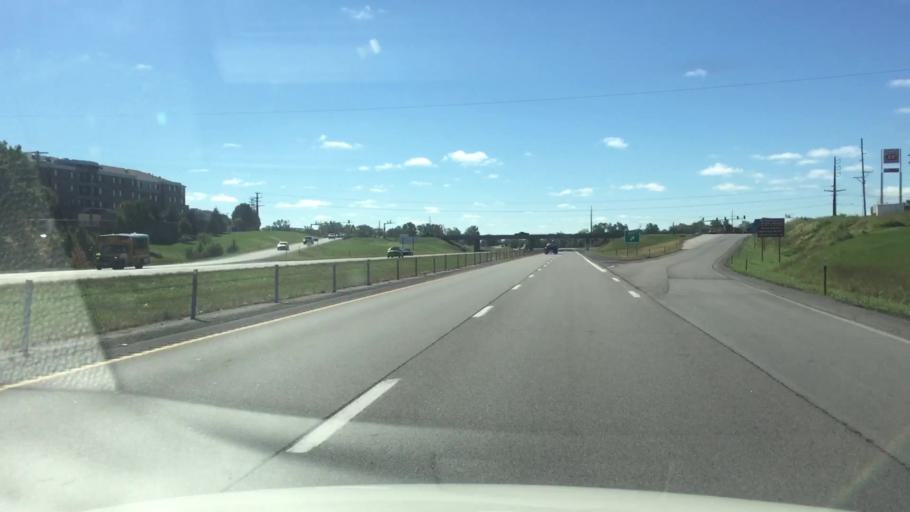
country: US
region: Missouri
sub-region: Boone County
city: Columbia
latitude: 38.9161
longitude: -92.2940
